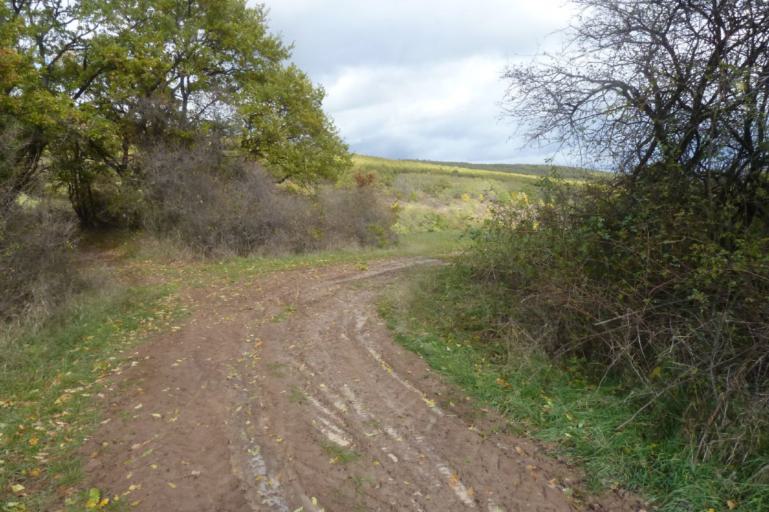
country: HU
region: Heves
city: Apc
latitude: 47.8178
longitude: 19.7205
